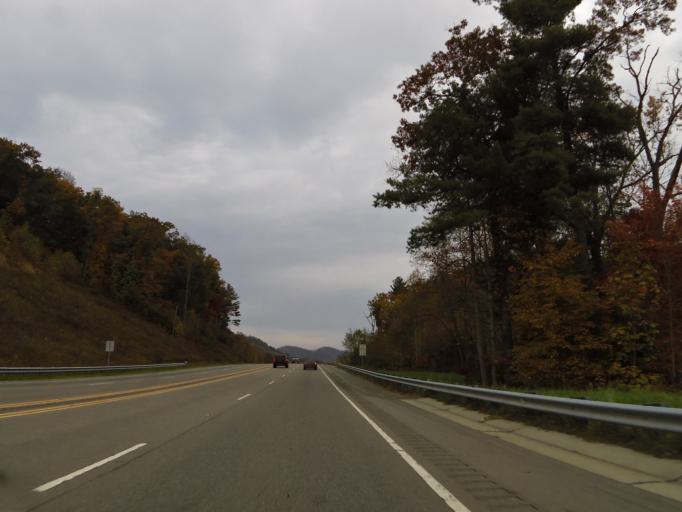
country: US
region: North Carolina
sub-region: Watauga County
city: Blowing Rock
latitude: 36.0592
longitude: -81.6020
